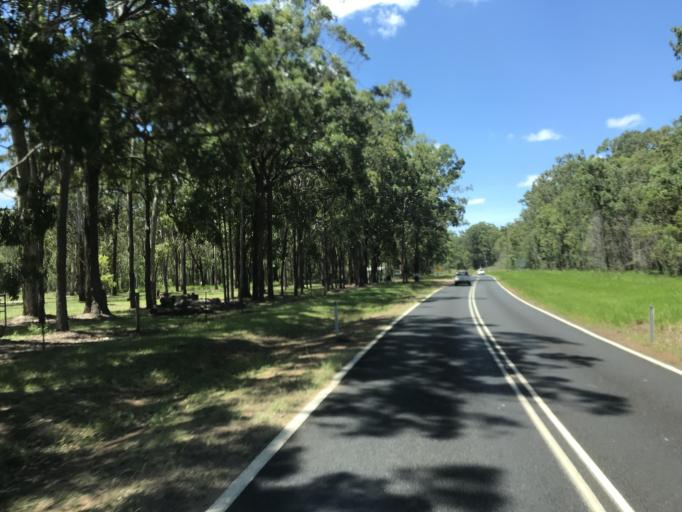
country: AU
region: Queensland
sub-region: Tablelands
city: Atherton
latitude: -17.4286
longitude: 145.3988
